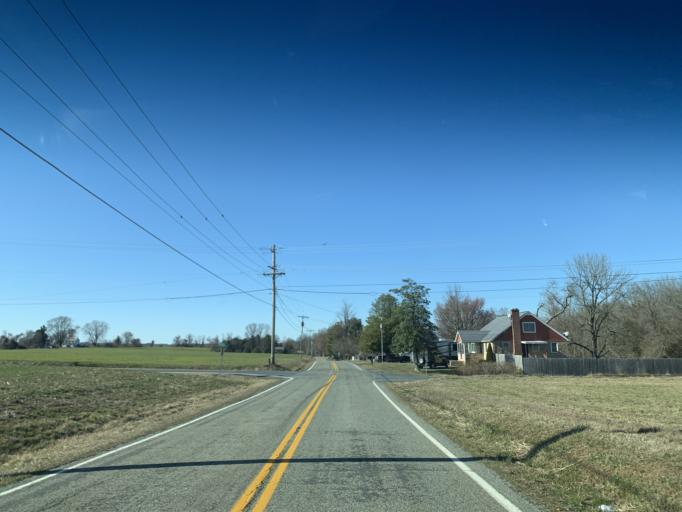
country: US
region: Maryland
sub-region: Cecil County
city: Rising Sun
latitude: 39.6814
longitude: -76.1000
